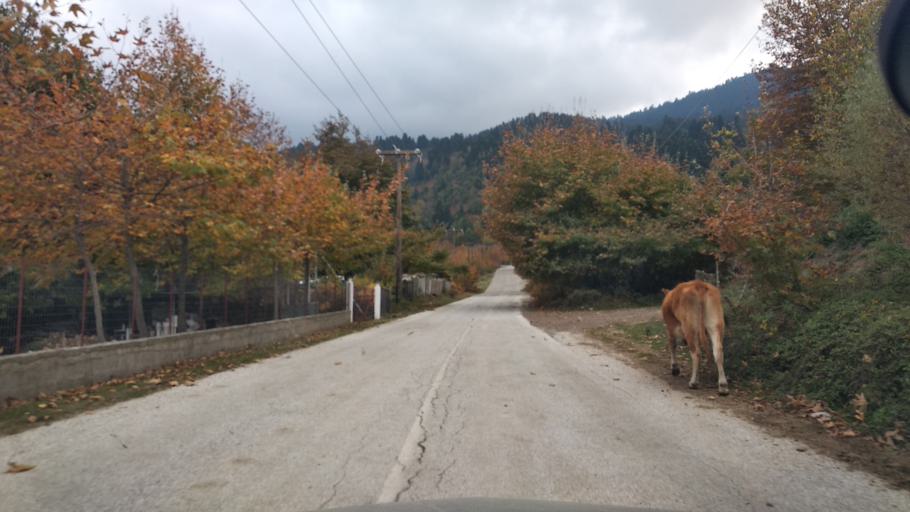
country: GR
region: Thessaly
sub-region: Trikala
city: Kalampaka
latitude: 39.5912
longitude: 21.4937
